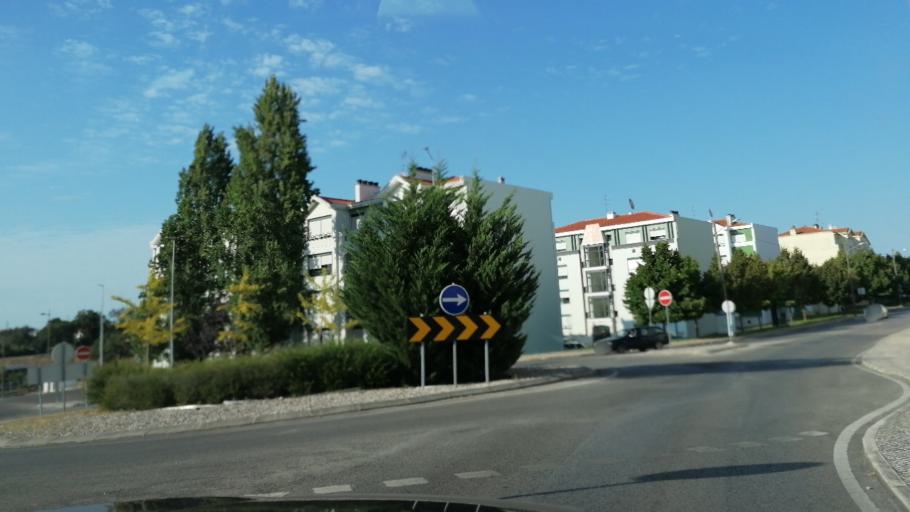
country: PT
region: Santarem
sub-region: Santarem
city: Santarem
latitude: 39.2493
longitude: -8.6874
